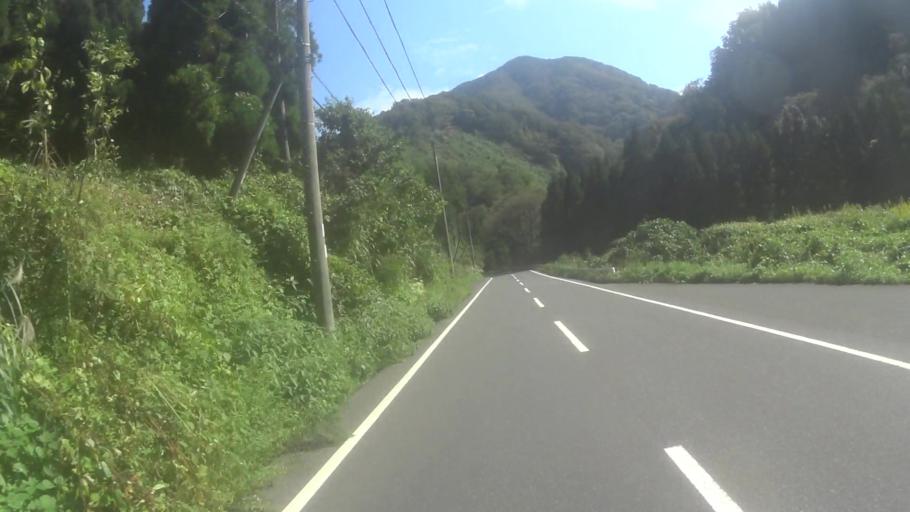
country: JP
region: Kyoto
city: Miyazu
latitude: 35.6400
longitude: 135.1279
